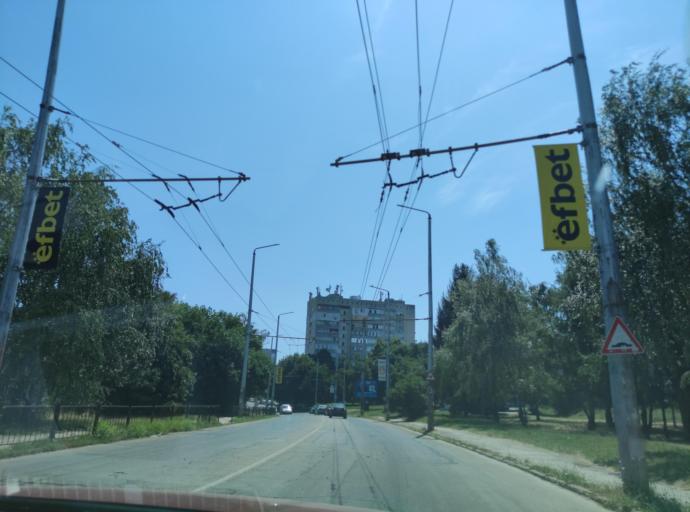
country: BG
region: Pleven
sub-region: Obshtina Pleven
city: Pleven
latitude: 43.4244
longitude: 24.5919
